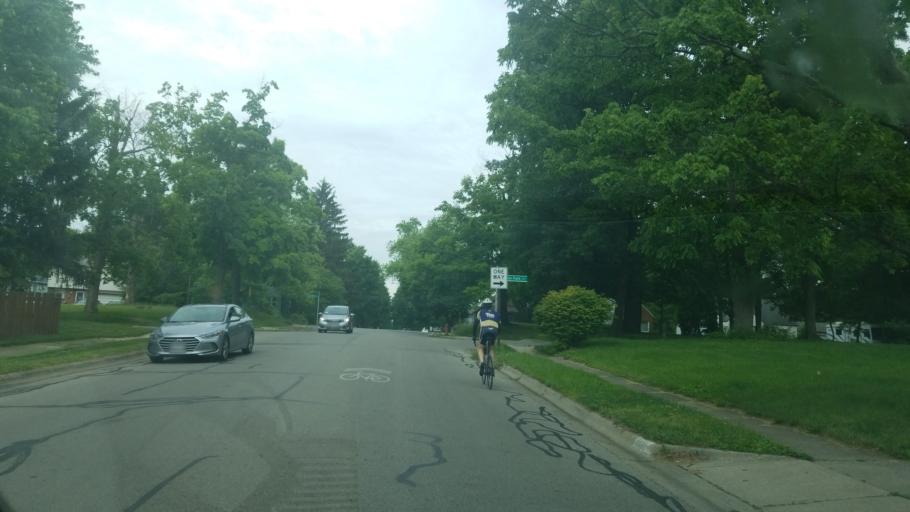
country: US
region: Ohio
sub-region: Franklin County
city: Worthington
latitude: 40.0751
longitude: -83.0071
